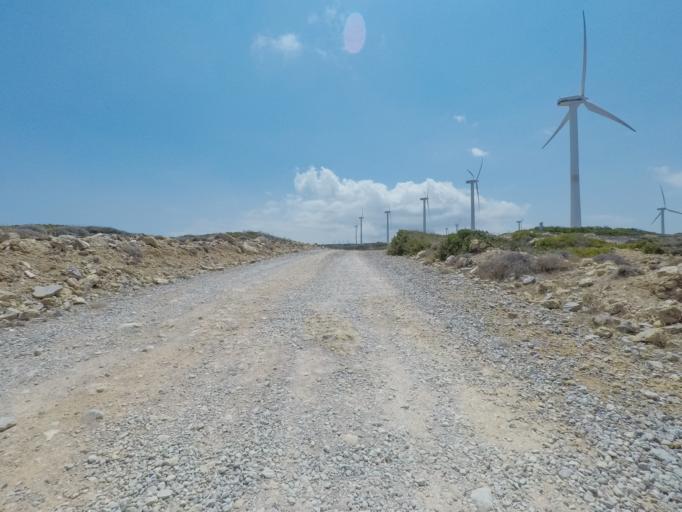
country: GR
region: Crete
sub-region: Nomos Lasithiou
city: Elounda
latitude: 35.3296
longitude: 25.7591
